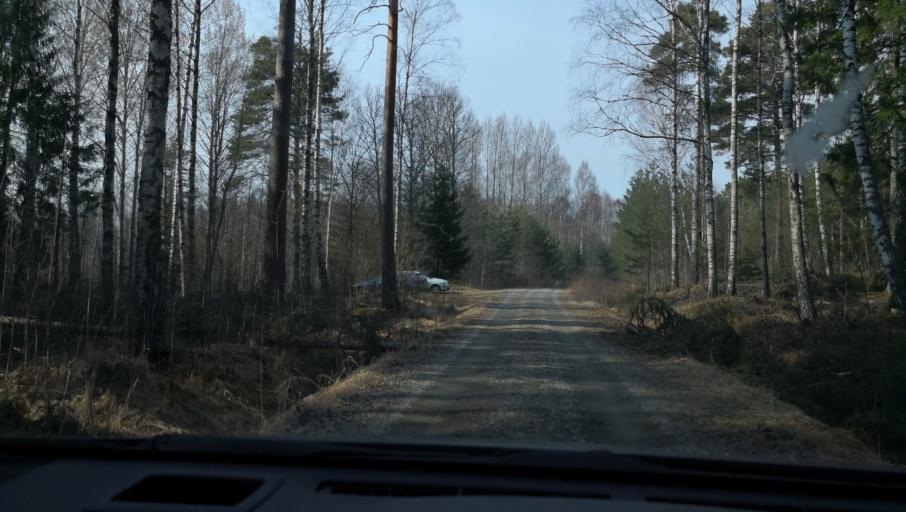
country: SE
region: OErebro
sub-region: Lindesbergs Kommun
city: Frovi
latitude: 59.3801
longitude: 15.4163
